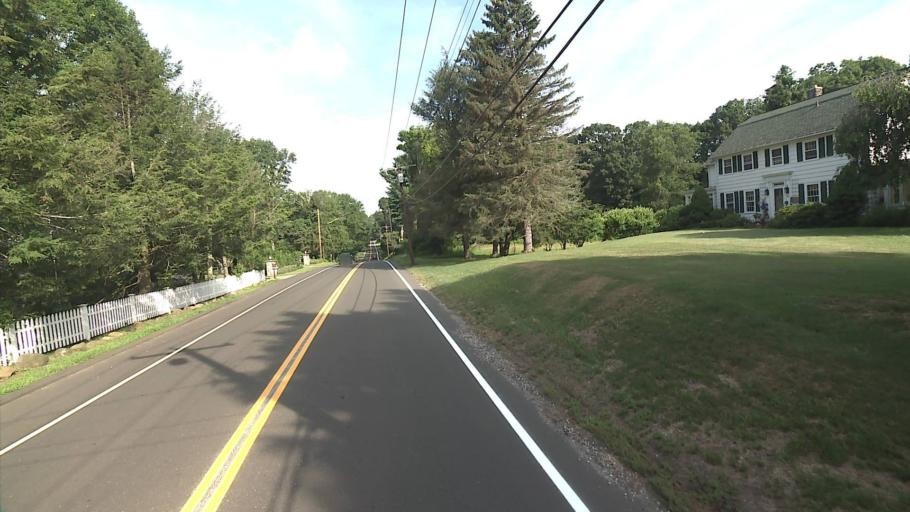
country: US
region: Connecticut
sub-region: New Haven County
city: Woodbridge
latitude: 41.3352
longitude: -73.0011
